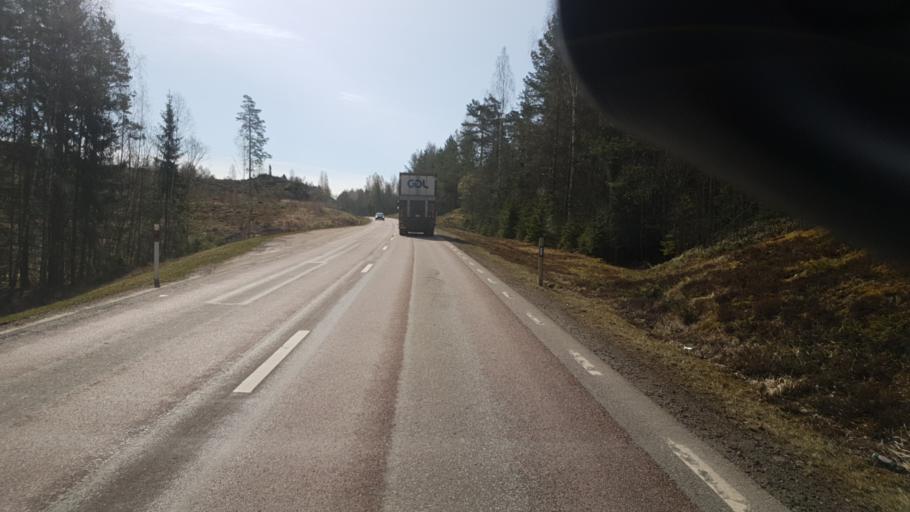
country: SE
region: Vaermland
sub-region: Arvika Kommun
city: Arvika
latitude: 59.5508
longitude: 12.7303
